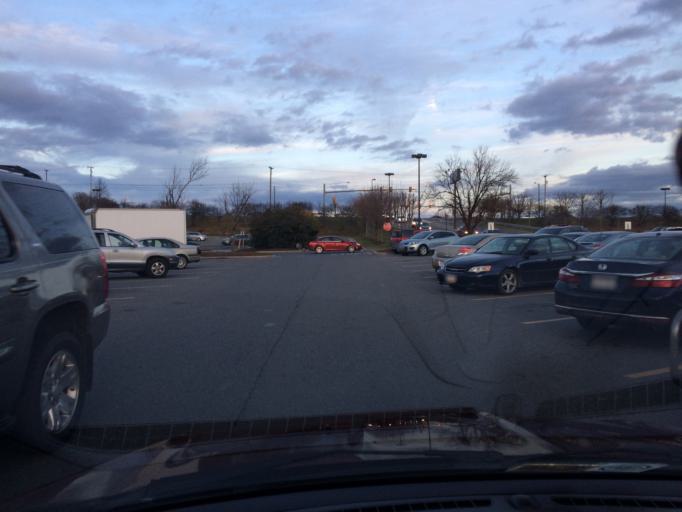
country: US
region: Virginia
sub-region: Montgomery County
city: Merrimac
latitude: 37.1611
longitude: -80.4246
